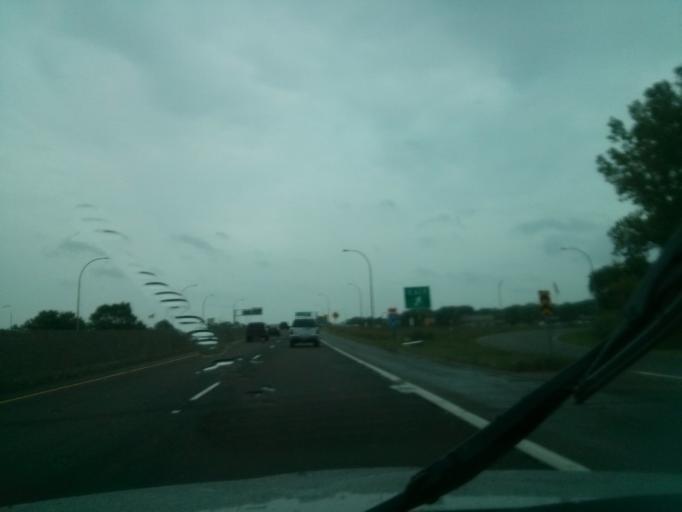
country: US
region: Minnesota
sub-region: Ramsey County
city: Little Canada
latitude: 45.0117
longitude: -93.0583
